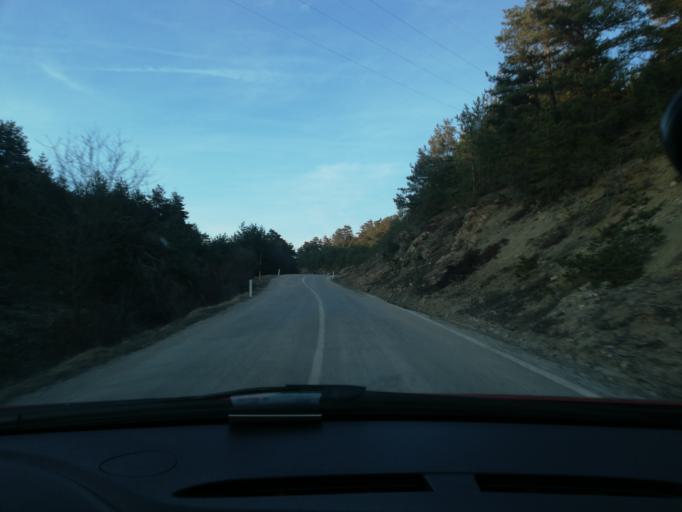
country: TR
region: Kastamonu
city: Agli
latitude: 41.7093
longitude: 33.6527
